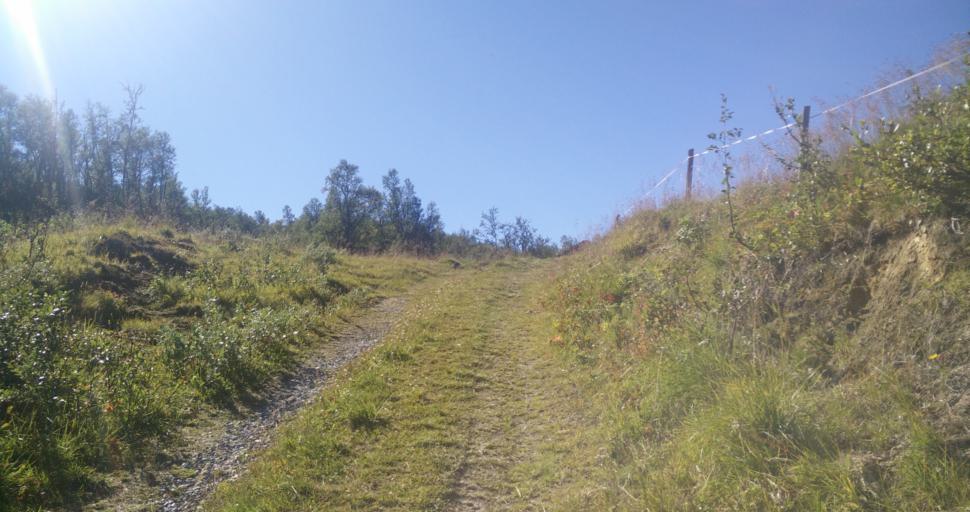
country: NO
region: Sor-Trondelag
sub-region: Tydal
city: Aas
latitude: 62.7137
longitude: 12.4596
